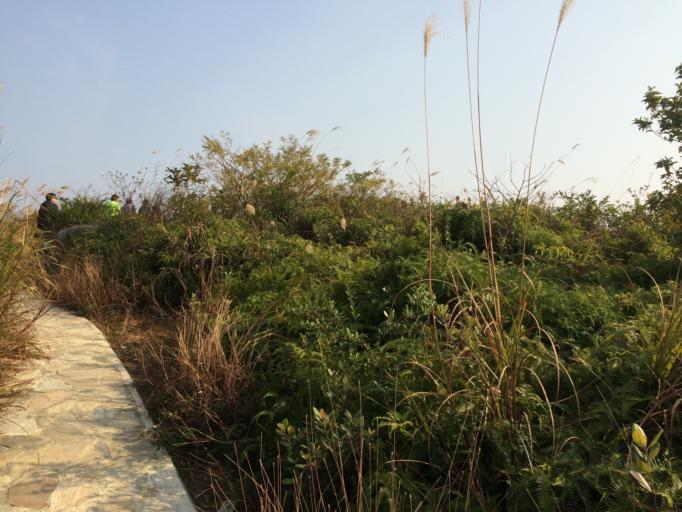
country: HK
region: Tai Po
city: Tai Po
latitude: 22.4505
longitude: 114.2191
